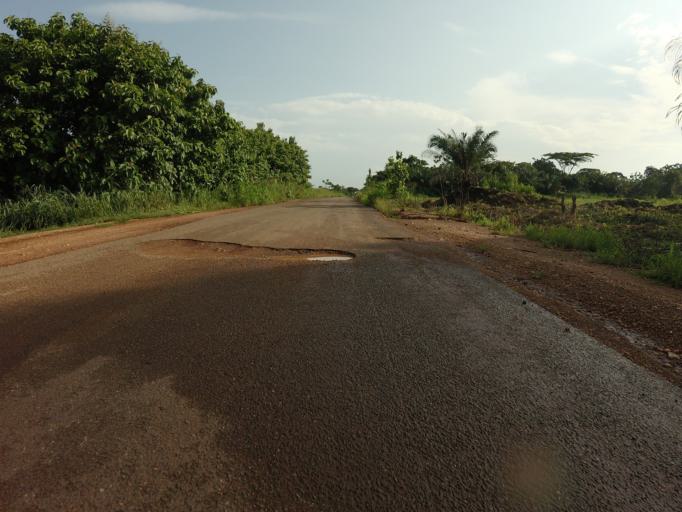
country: GH
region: Volta
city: Hohoe
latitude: 7.0826
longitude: 0.4431
